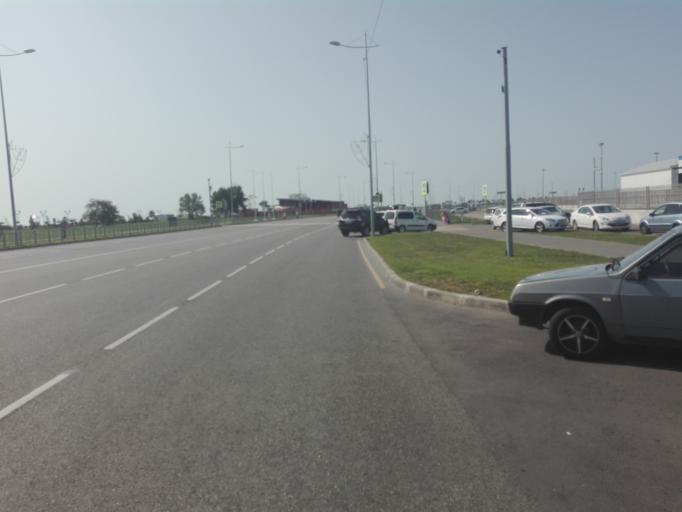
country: RU
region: Krasnodarskiy
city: Adler
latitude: 43.3996
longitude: 39.9538
